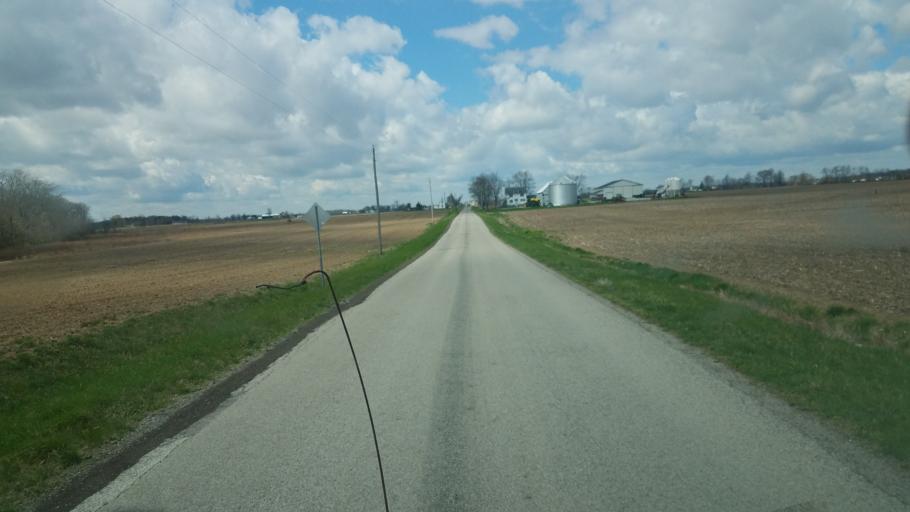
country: US
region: Ohio
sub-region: Union County
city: Richwood
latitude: 40.3937
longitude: -83.2913
